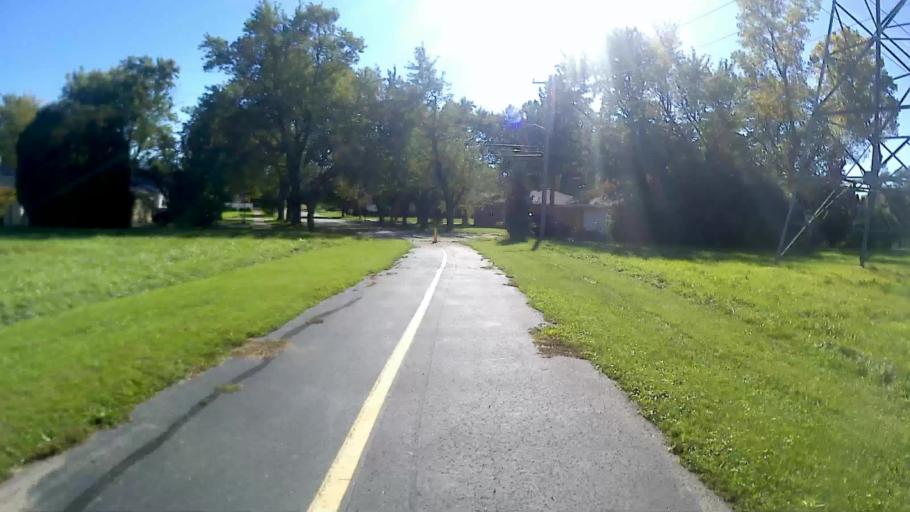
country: US
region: Illinois
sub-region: DuPage County
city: Wood Dale
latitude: 41.9561
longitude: -87.9959
